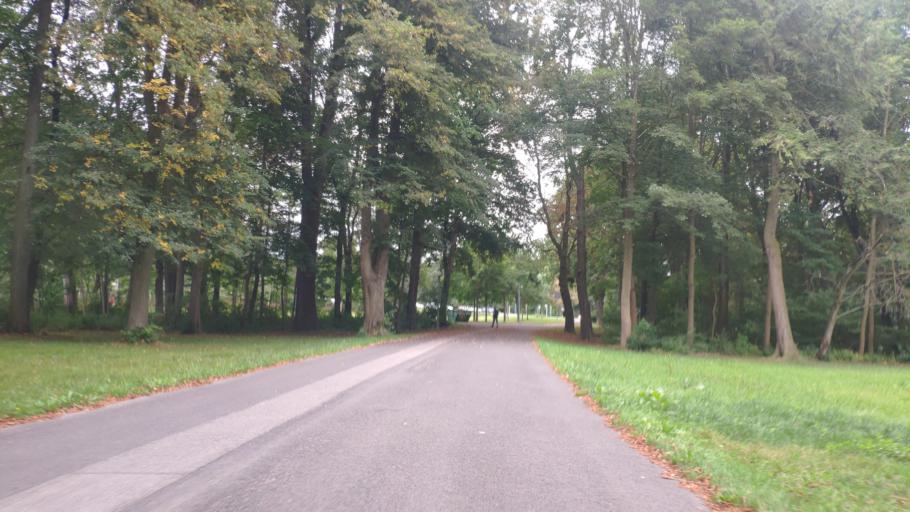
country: DE
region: Saxony
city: Chemnitz
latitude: 50.7982
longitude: 12.9084
